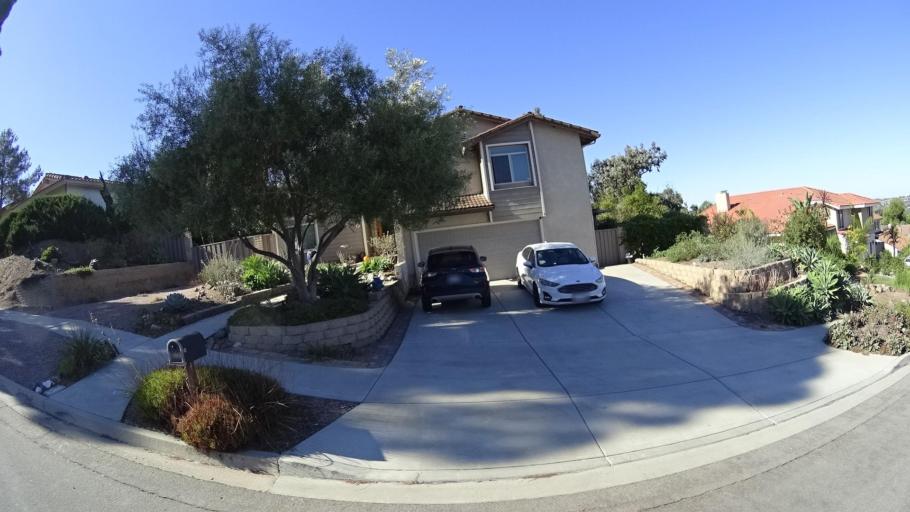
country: US
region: California
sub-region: San Diego County
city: Bonita
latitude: 32.6651
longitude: -116.9980
